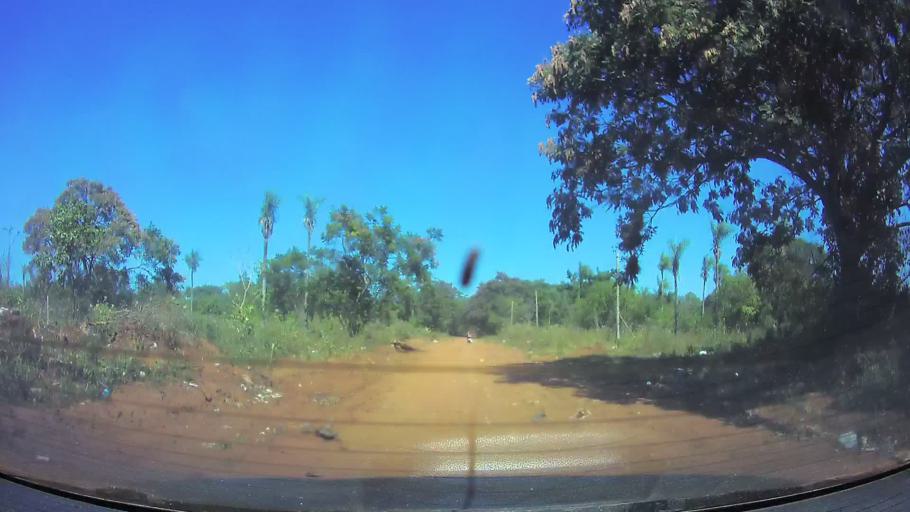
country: PY
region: Central
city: Limpio
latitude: -25.2407
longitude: -57.4533
